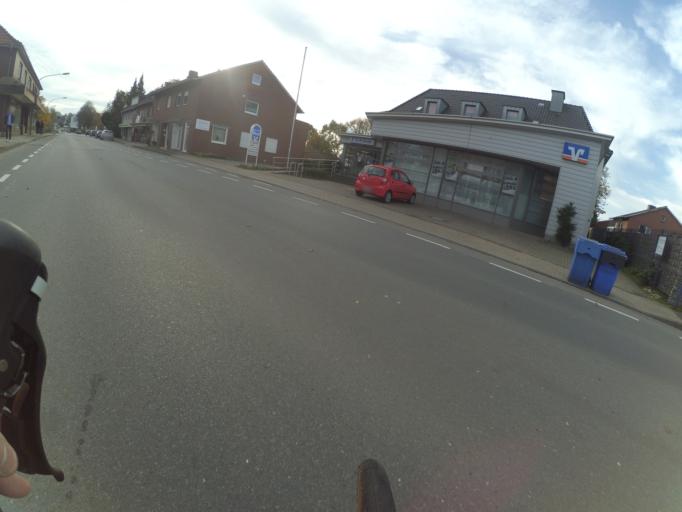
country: DE
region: North Rhine-Westphalia
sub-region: Regierungsbezirk Munster
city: Tecklenburg
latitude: 52.2636
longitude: 7.7894
